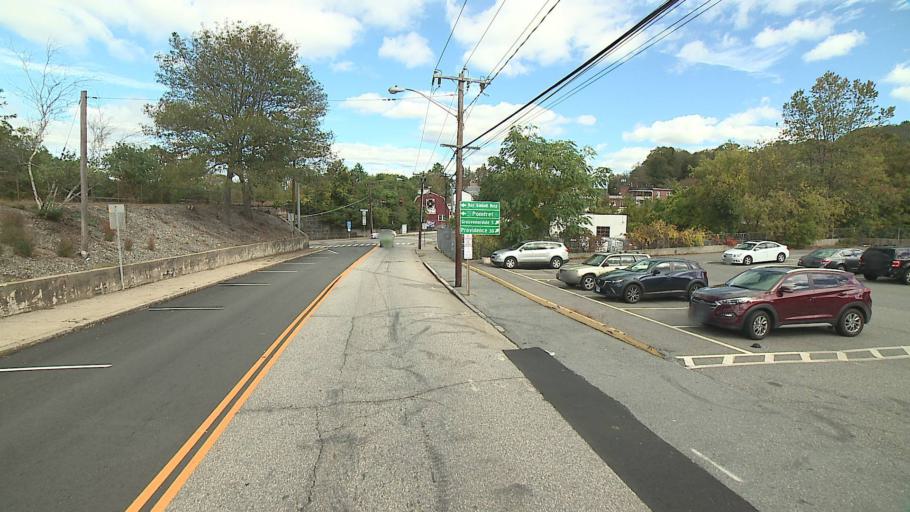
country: US
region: Connecticut
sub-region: Windham County
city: Putnam
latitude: 41.9150
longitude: -71.9076
